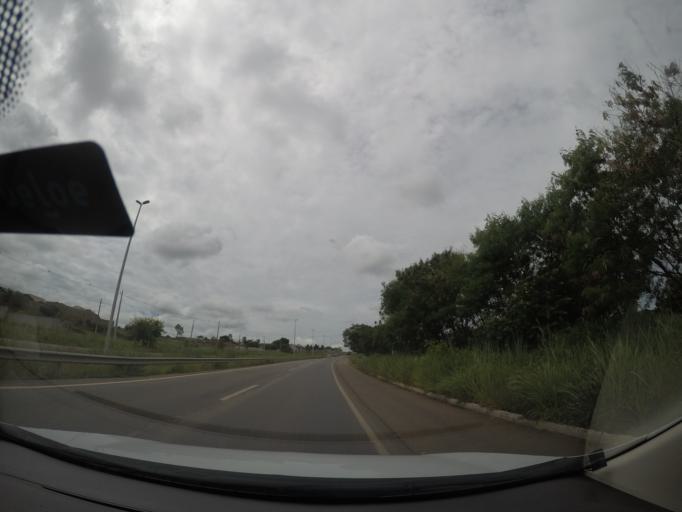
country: BR
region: Goias
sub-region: Inhumas
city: Inhumas
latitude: -16.3743
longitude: -49.5018
